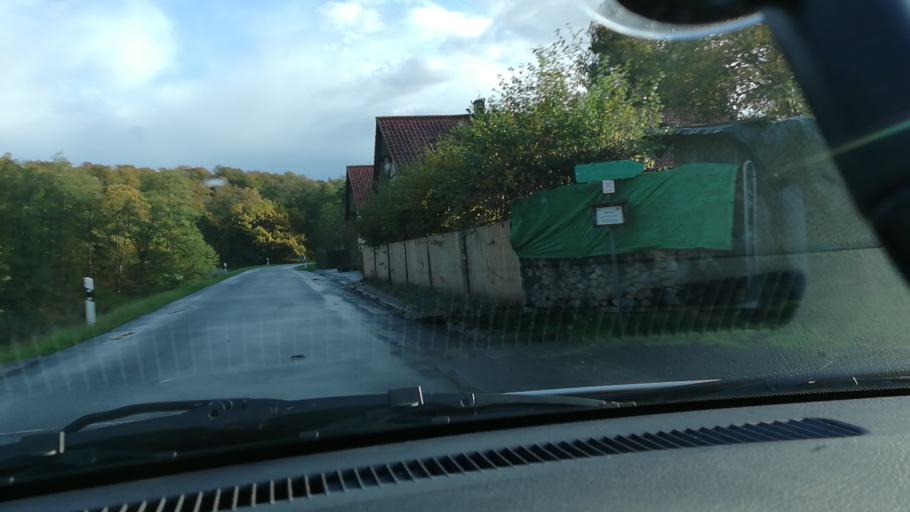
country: DE
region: Bavaria
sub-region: Regierungsbezirk Unterfranken
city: Rechtenbach
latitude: 49.9278
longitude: 9.5033
